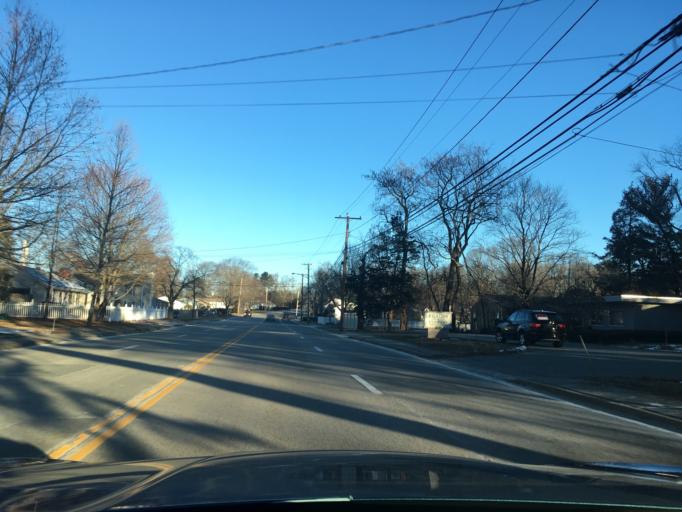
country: US
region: Rhode Island
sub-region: Kent County
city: Warwick
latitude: 41.7083
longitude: -71.4637
